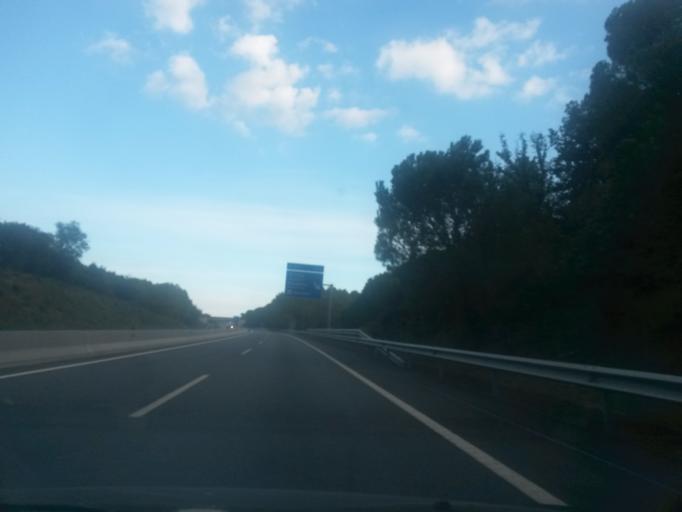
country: ES
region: Catalonia
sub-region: Provincia de Girona
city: Vilobi d'Onyar
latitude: 41.8761
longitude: 2.7444
